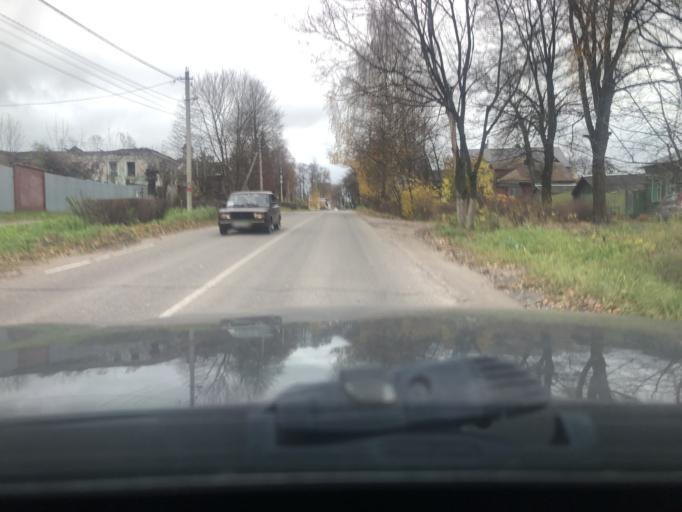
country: RU
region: Moskovskaya
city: Sergiyev Posad
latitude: 56.3019
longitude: 38.1241
